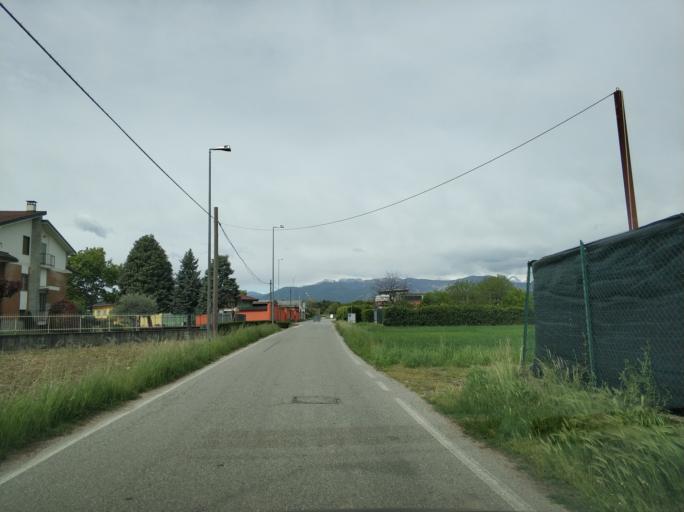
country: IT
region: Piedmont
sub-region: Provincia di Torino
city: Caselle Torinese
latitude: 45.1654
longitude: 7.6510
